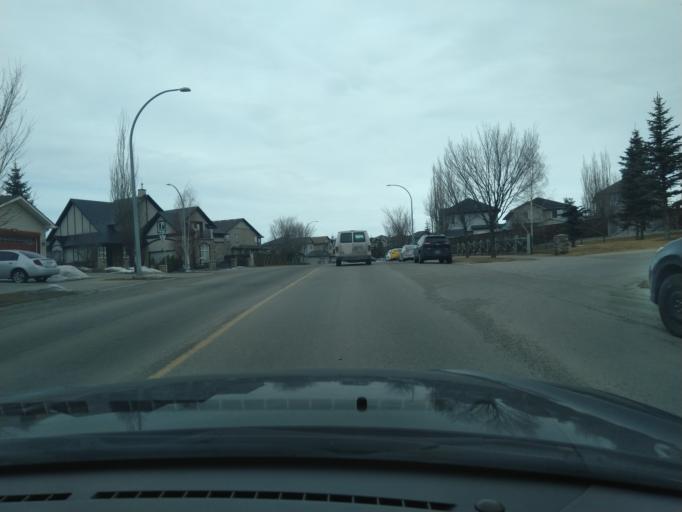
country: CA
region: Alberta
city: Calgary
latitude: 51.1610
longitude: -114.1016
